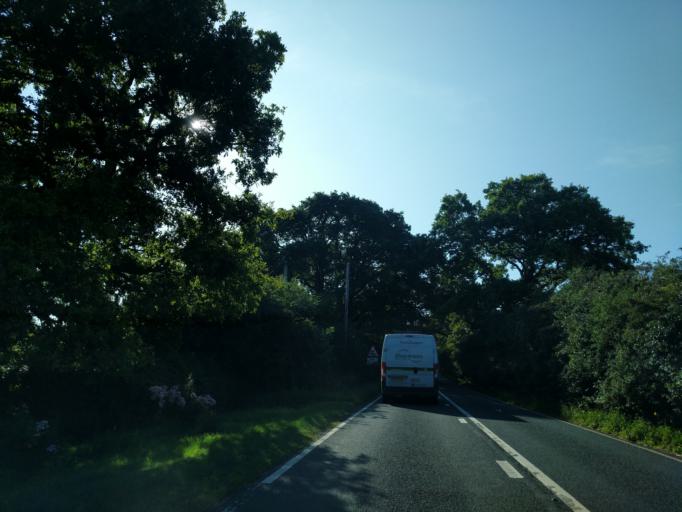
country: GB
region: England
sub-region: Lincolnshire
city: Bourne
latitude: 52.8005
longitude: -0.4721
